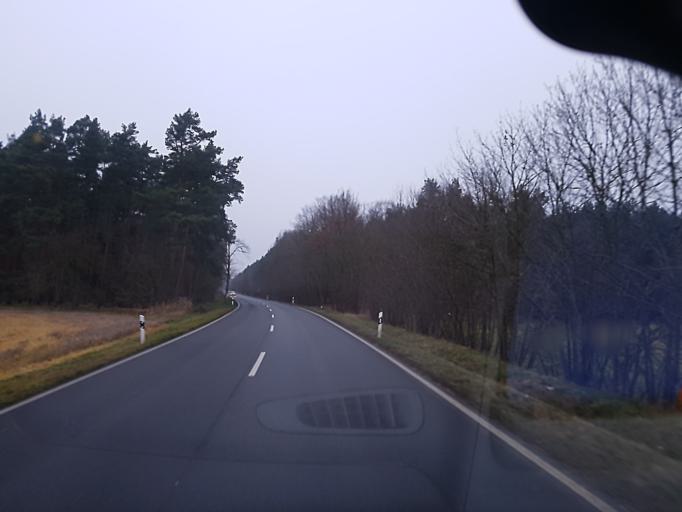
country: DE
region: Brandenburg
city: Luebben
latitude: 51.8912
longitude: 13.9002
